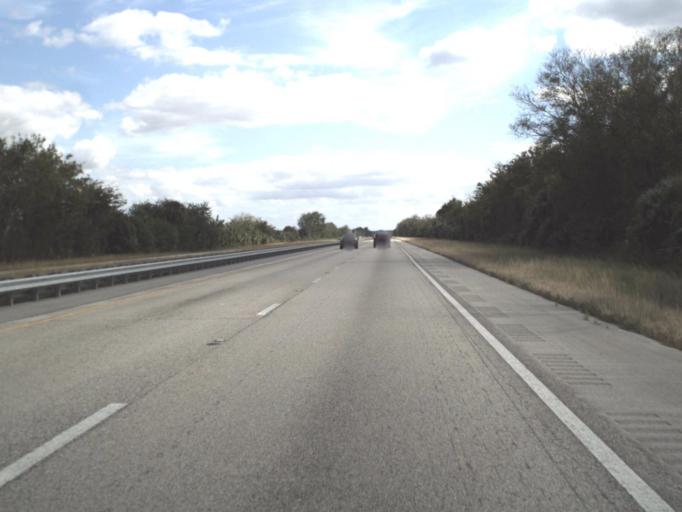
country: US
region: Florida
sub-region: Brevard County
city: Port Saint John
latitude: 28.4446
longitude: -80.8676
